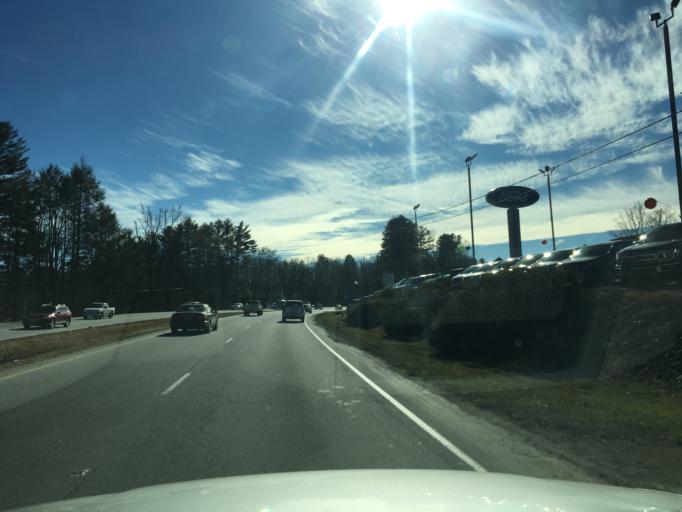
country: US
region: North Carolina
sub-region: Transylvania County
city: Brevard
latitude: 35.2594
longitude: -82.7161
